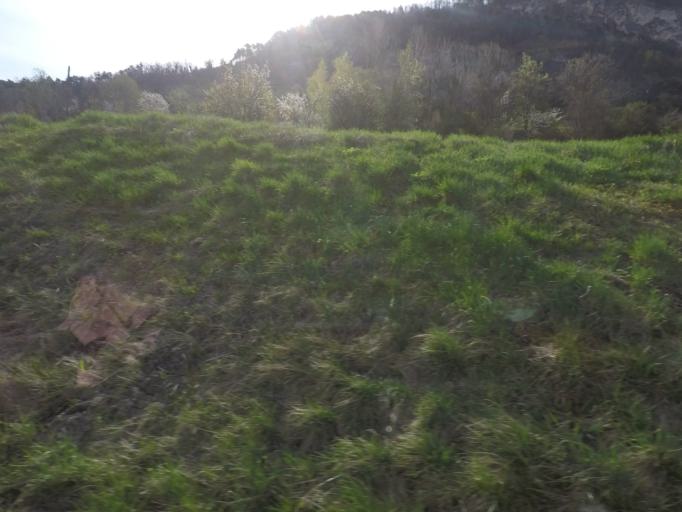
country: CH
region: Valais
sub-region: Herens District
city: Vex
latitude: 46.2236
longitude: 7.3911
